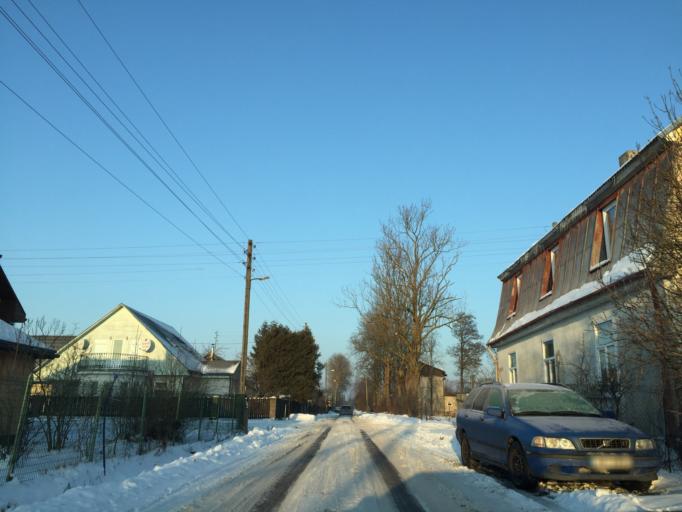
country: LV
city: Tireli
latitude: 56.9397
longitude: 23.6110
